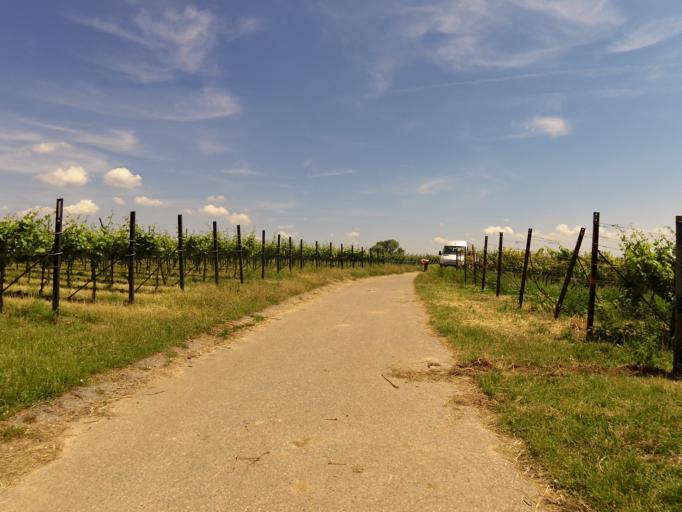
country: DE
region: Rheinland-Pfalz
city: Bochingen
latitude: 49.2125
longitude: 8.0924
